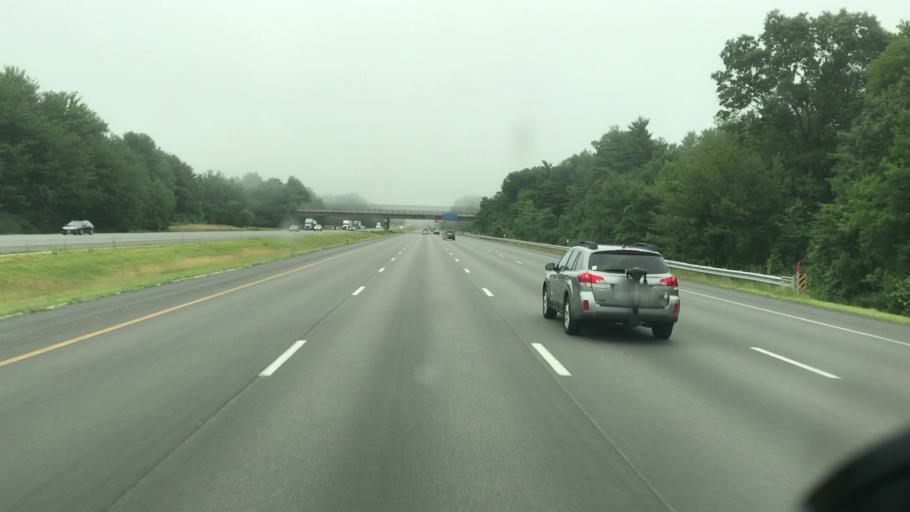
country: US
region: New Hampshire
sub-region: Rockingham County
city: Hampton Falls
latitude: 42.9173
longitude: -70.8711
